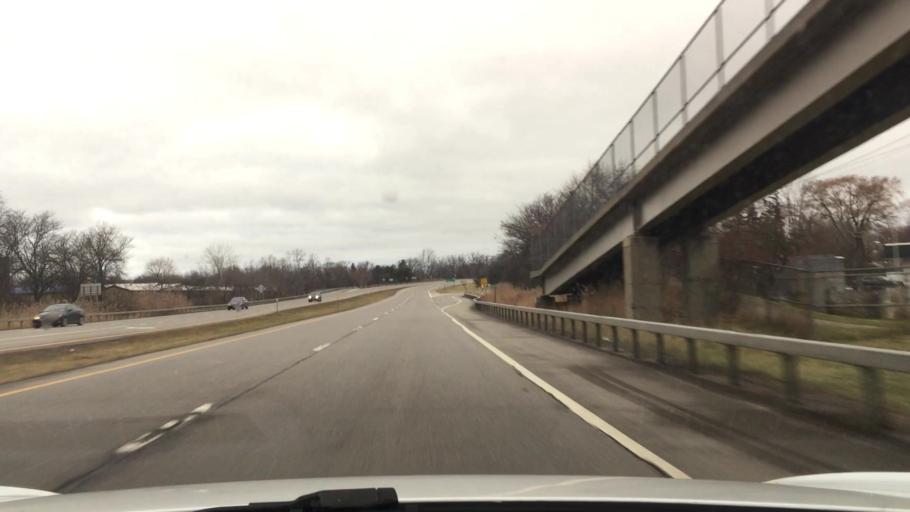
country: US
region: New York
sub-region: Erie County
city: Tonawanda
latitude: 43.0080
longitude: -78.8602
